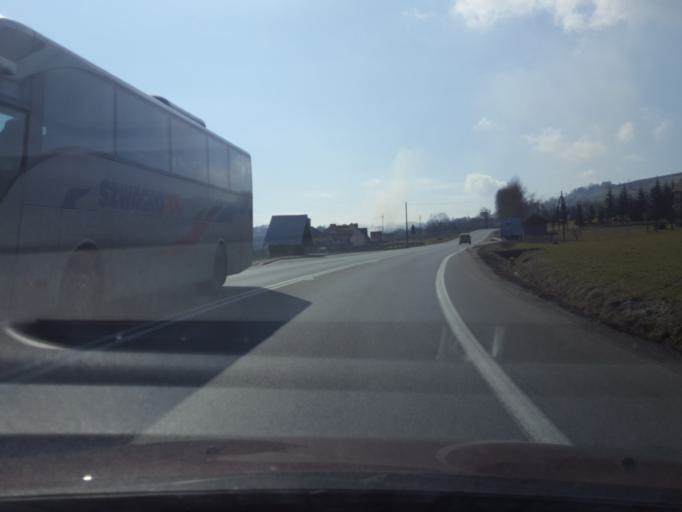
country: PL
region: Lesser Poland Voivodeship
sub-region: Powiat nowosadecki
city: Lososina Dolna
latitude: 49.7375
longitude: 20.6374
